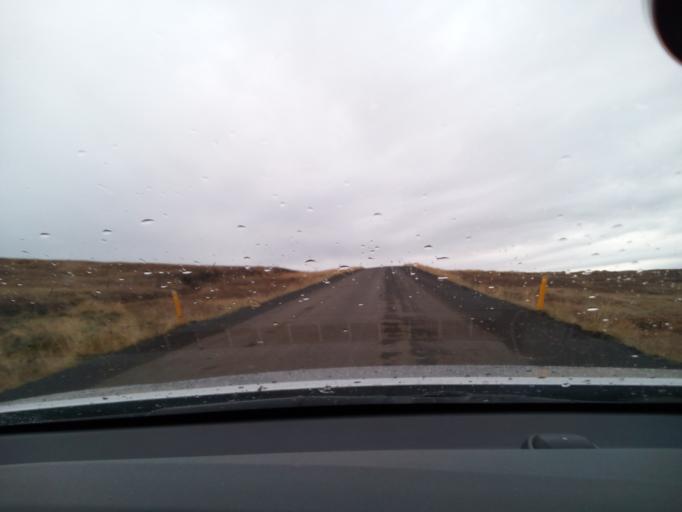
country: IS
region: Northeast
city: Laugar
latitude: 65.7895
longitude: -17.2282
